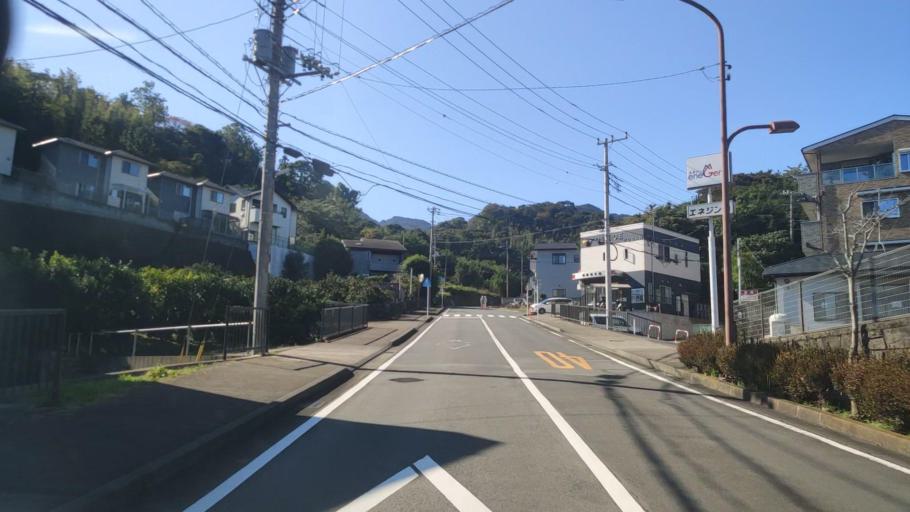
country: JP
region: Shizuoka
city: Atami
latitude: 35.0468
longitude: 139.0670
